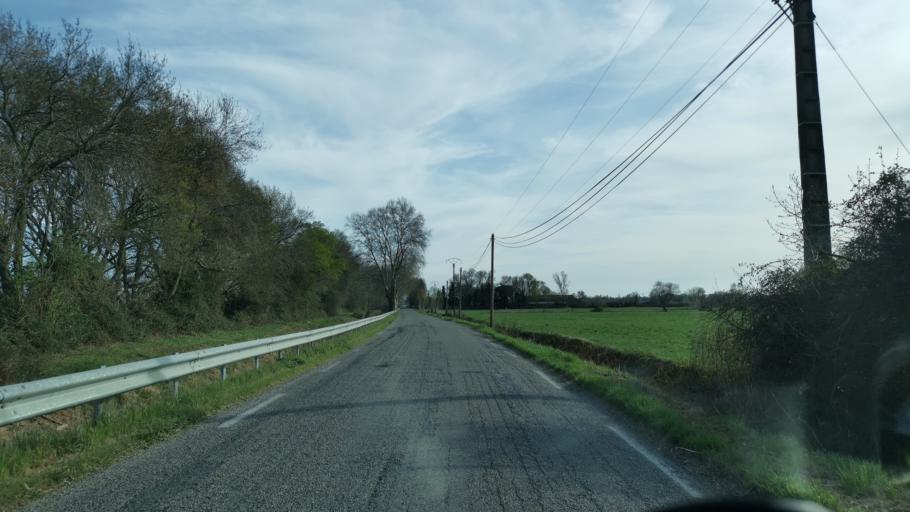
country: FR
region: Provence-Alpes-Cote d'Azur
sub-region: Departement des Bouches-du-Rhone
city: Arles
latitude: 43.6371
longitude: 4.7097
